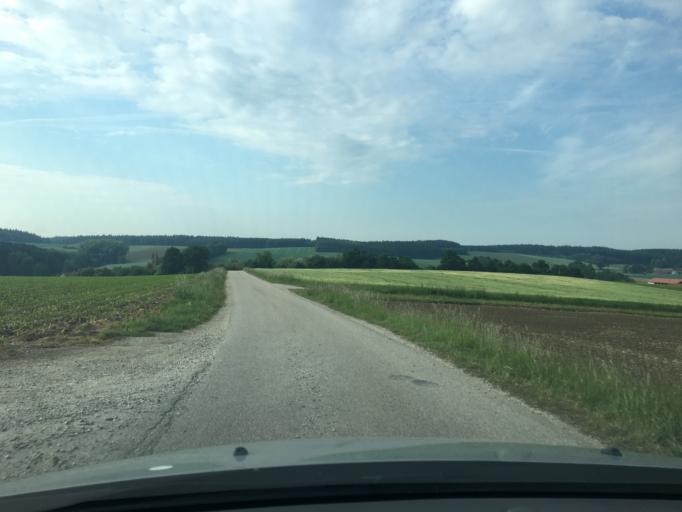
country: DE
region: Bavaria
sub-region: Upper Bavaria
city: Egglkofen
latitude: 48.4020
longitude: 12.4267
